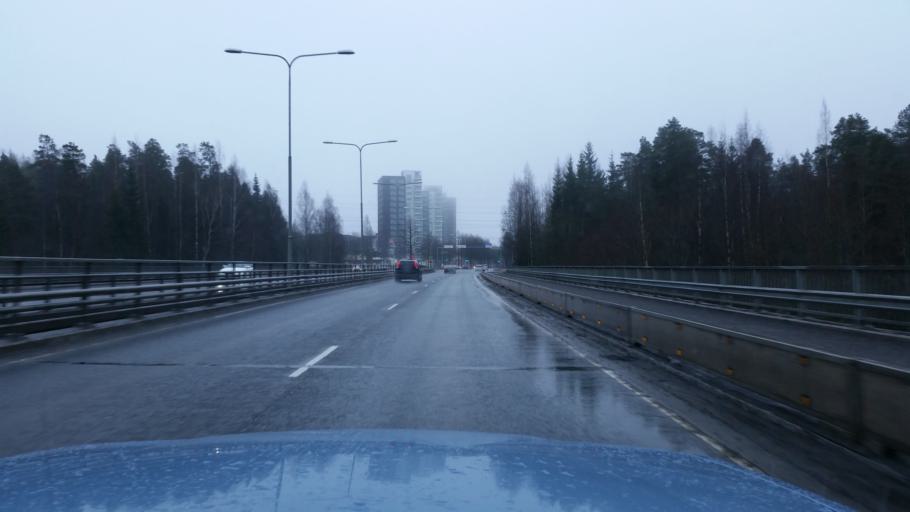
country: FI
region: Pirkanmaa
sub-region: Tampere
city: Tampere
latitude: 61.4608
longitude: 23.8450
